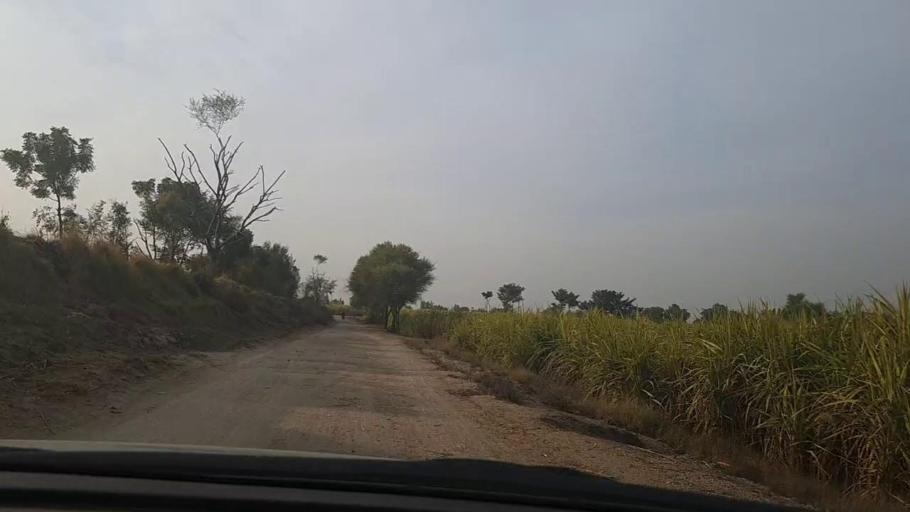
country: PK
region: Sindh
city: Daulatpur
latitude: 26.3334
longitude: 68.0426
